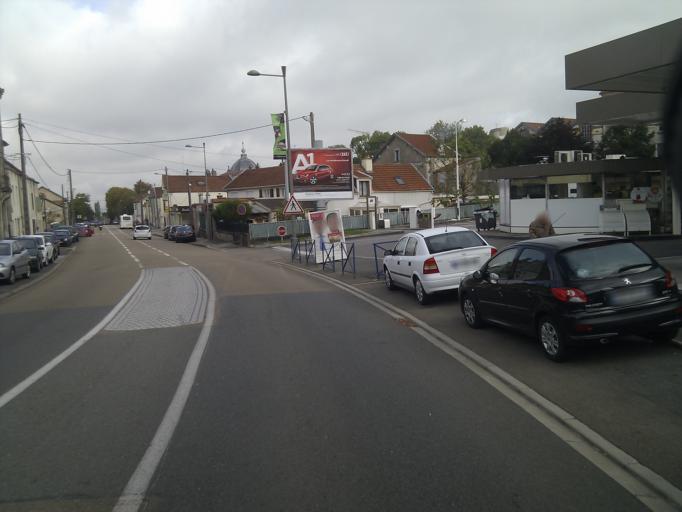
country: FR
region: Champagne-Ardenne
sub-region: Departement de la Haute-Marne
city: Chaumont
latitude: 48.1174
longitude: 5.1405
